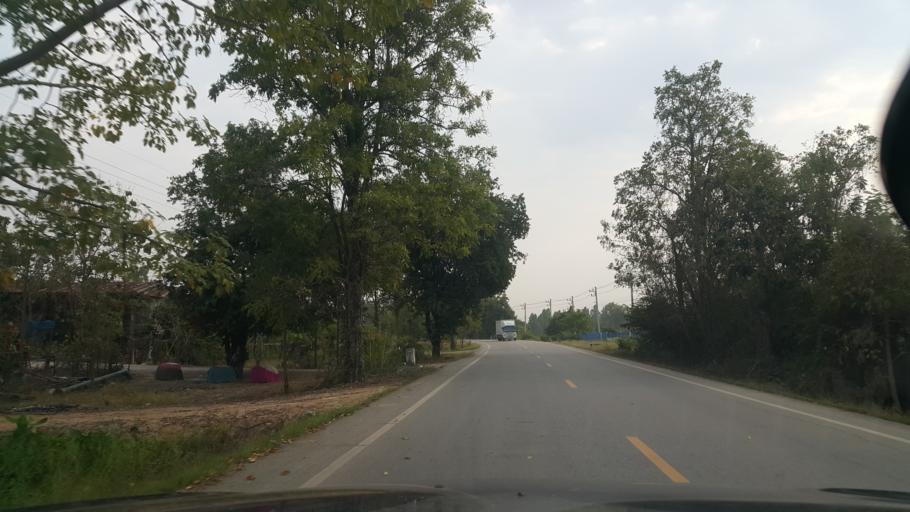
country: TH
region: Sukhothai
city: Si Samrong
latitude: 17.1715
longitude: 99.7285
